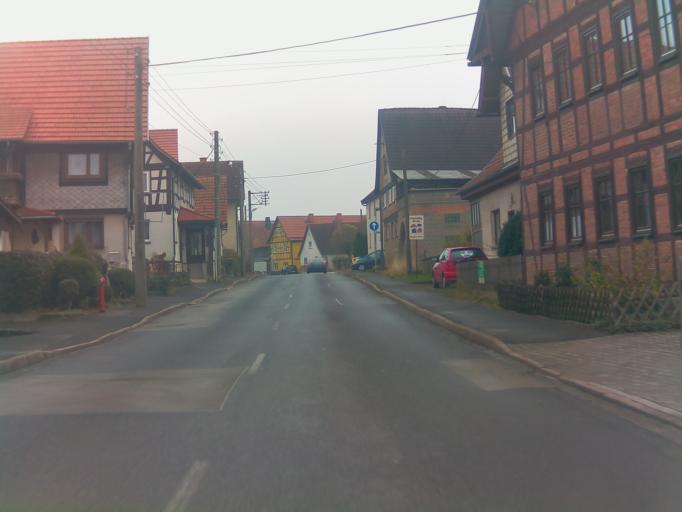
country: DE
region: Thuringia
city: Juchsen
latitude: 50.4573
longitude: 10.5437
